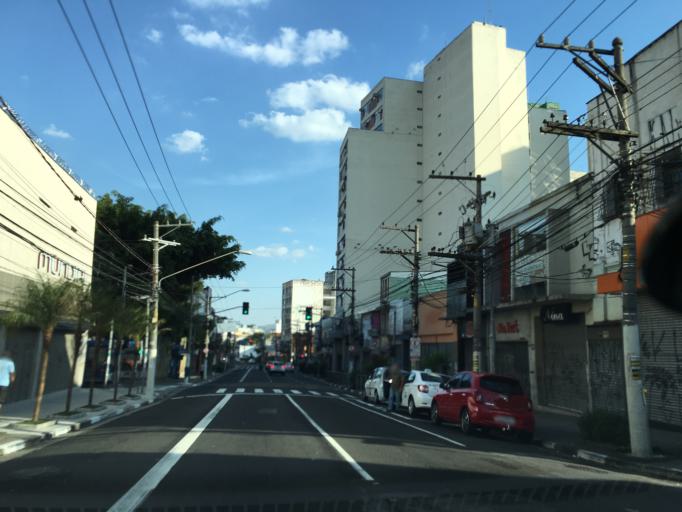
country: BR
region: Sao Paulo
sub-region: Sao Paulo
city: Sao Paulo
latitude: -23.5016
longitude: -46.6261
